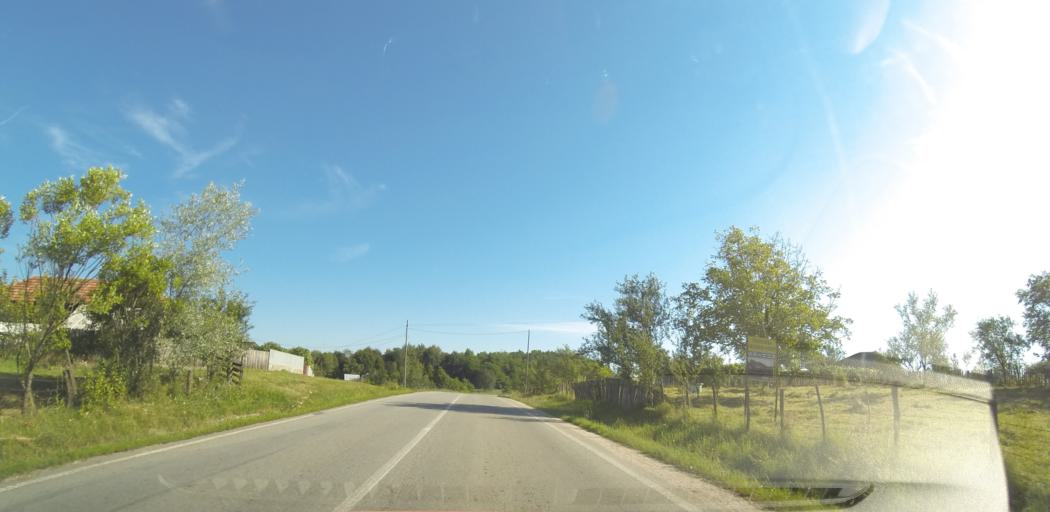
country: RO
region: Valcea
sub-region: Comuna Mateesti
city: Mateesti
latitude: 45.1288
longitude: 23.8536
